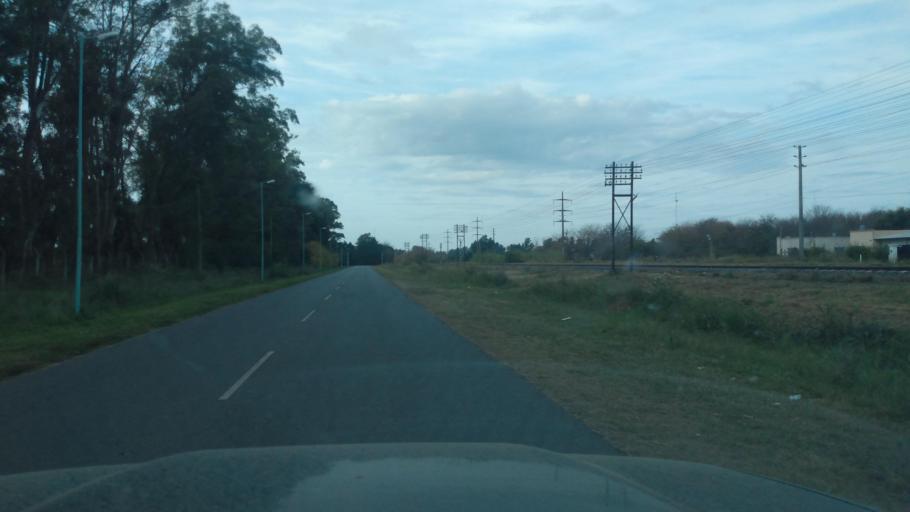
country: AR
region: Buenos Aires
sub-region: Partido de Lujan
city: Lujan
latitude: -34.5867
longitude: -59.1323
